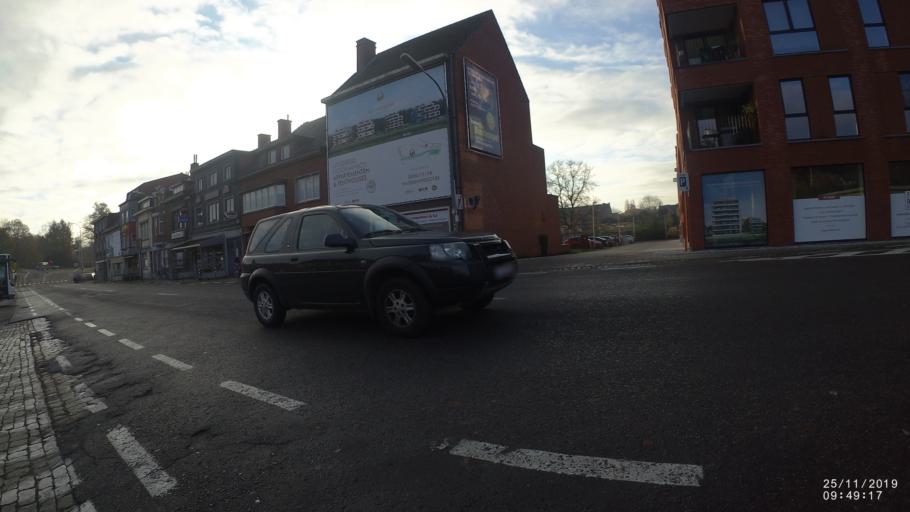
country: BE
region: Flanders
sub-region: Provincie Vlaams-Brabant
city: Diest
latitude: 50.9927
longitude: 5.0507
